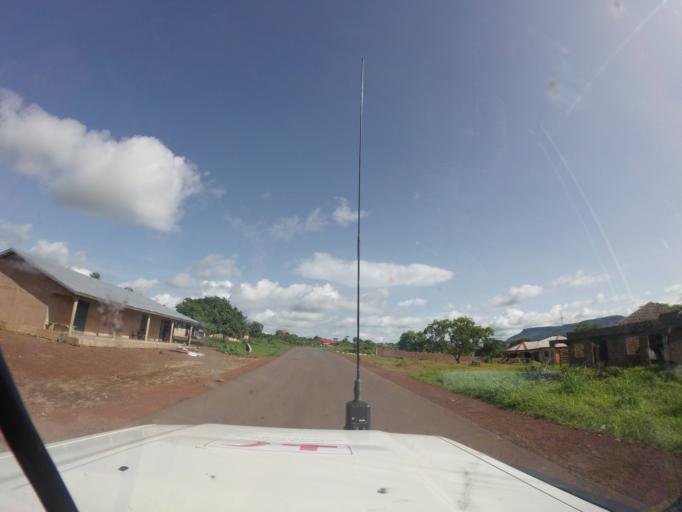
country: GN
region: Mamou
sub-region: Mamou Prefecture
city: Mamou
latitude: 10.2680
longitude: -12.4530
